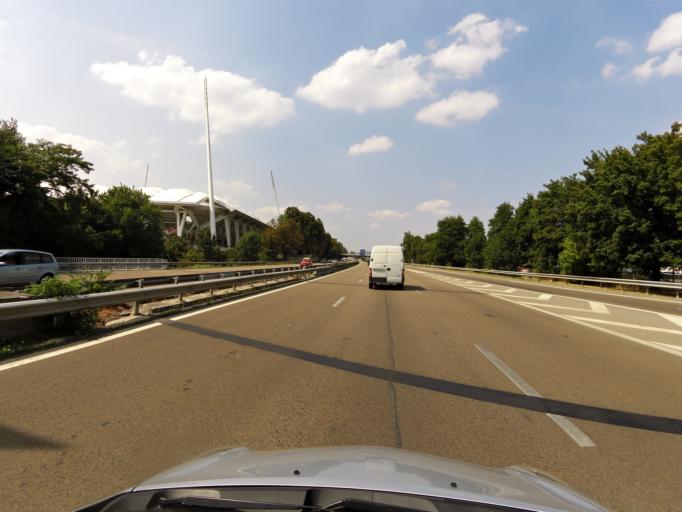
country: FR
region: Champagne-Ardenne
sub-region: Departement de la Marne
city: Reims
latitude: 49.2465
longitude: 4.0277
